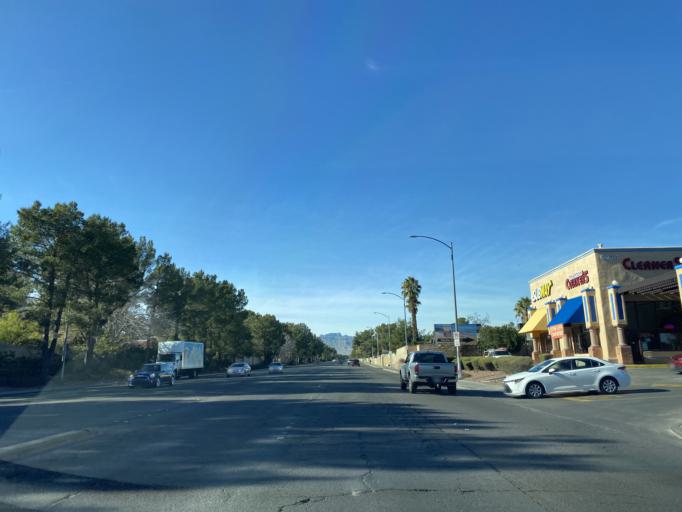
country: US
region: Nevada
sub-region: Clark County
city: Spring Valley
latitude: 36.0999
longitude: -115.2443
